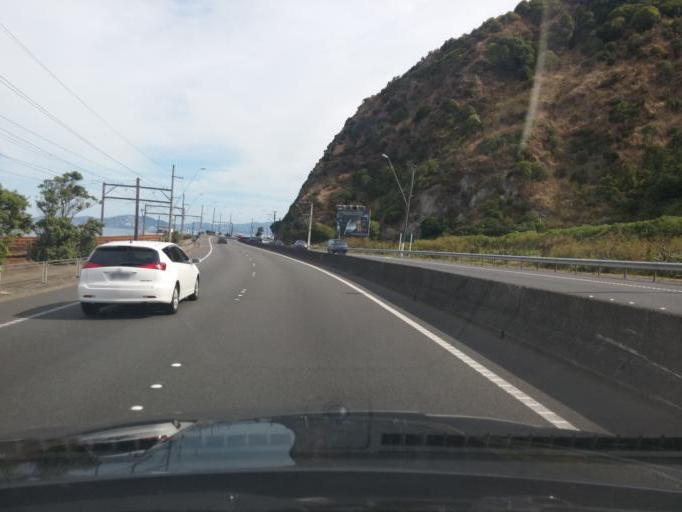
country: NZ
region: Wellington
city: Petone
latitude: -41.2293
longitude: 174.8428
